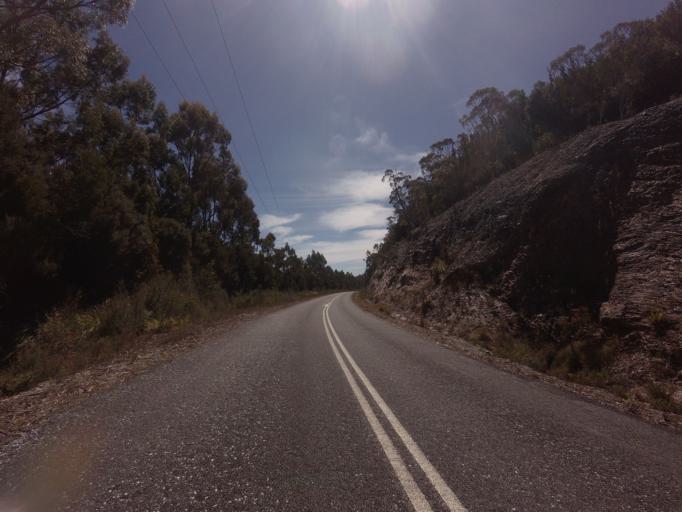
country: AU
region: Tasmania
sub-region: West Coast
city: Queenstown
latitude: -42.7814
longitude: 146.0303
